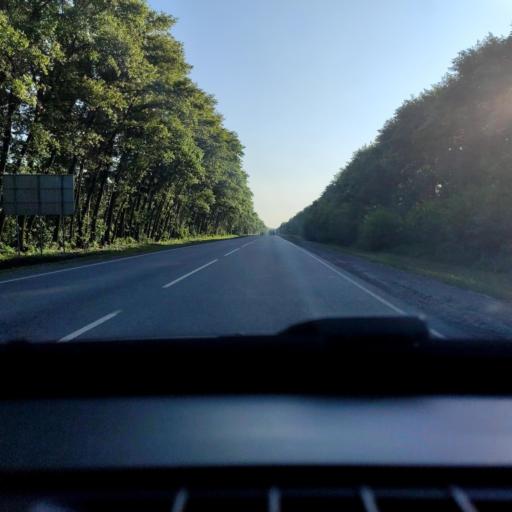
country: RU
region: Voronezj
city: Kashirskoye
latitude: 51.4660
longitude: 39.8589
